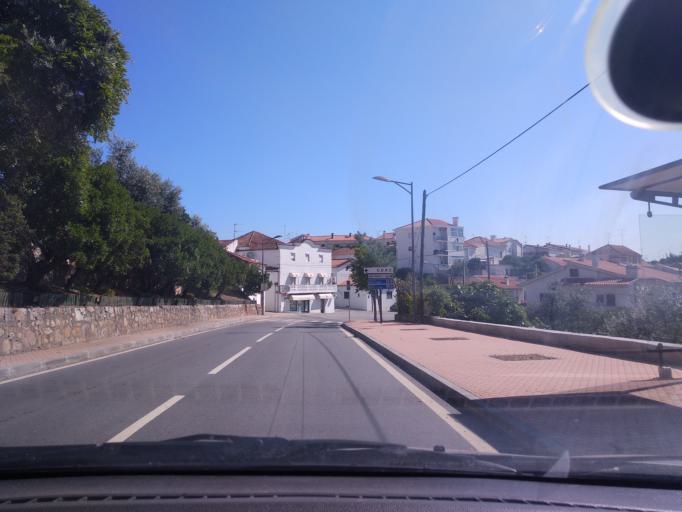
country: PT
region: Portalegre
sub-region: Nisa
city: Nisa
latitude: 39.6522
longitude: -7.6728
